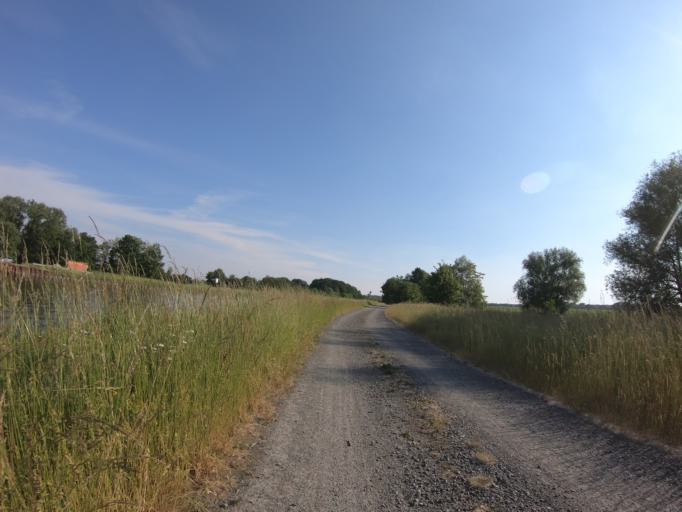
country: DE
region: Lower Saxony
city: Calberlah
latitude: 52.4063
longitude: 10.6183
